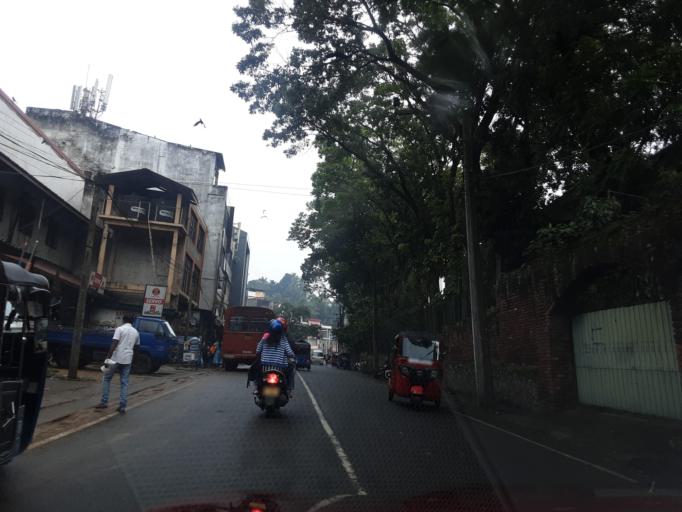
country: LK
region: Central
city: Kandy
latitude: 7.3208
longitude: 80.6247
